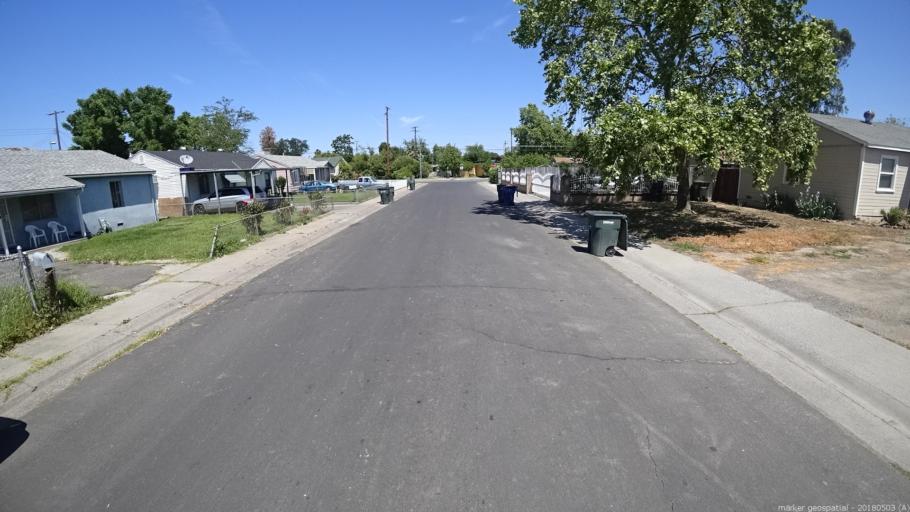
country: US
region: California
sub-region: Sacramento County
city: Rio Linda
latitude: 38.6394
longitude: -121.4266
